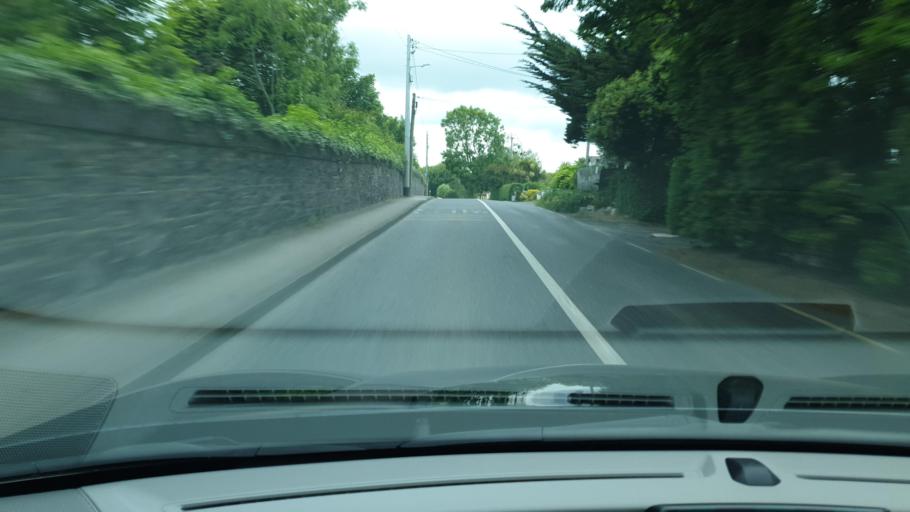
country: IE
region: Leinster
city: Balbriggan
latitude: 53.6023
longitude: -6.1669
